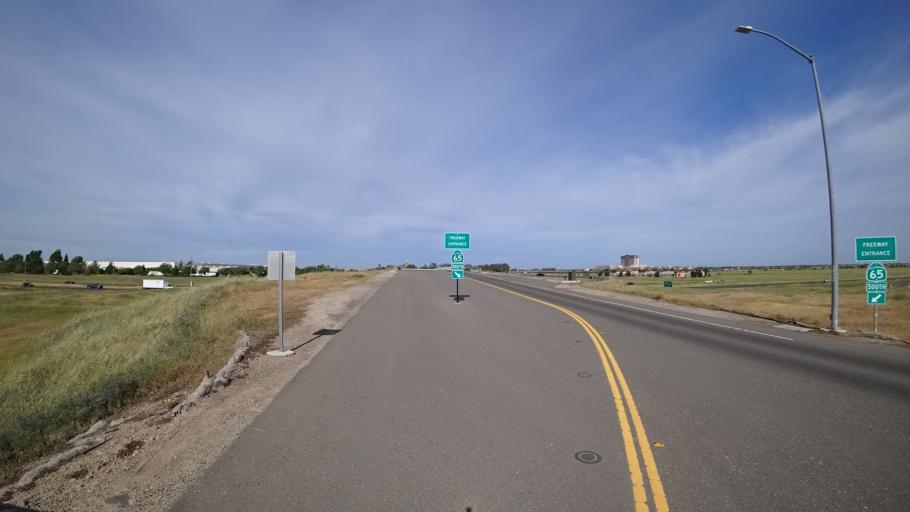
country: US
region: California
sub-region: Placer County
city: Lincoln
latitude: 38.8316
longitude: -121.2984
